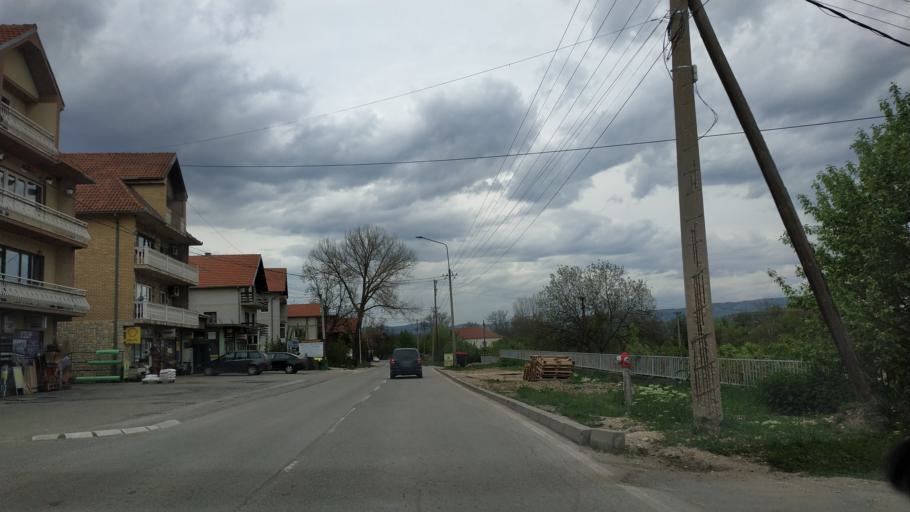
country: RS
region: Central Serbia
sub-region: Zajecarski Okrug
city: Soko Banja
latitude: 43.6492
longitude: 21.8592
